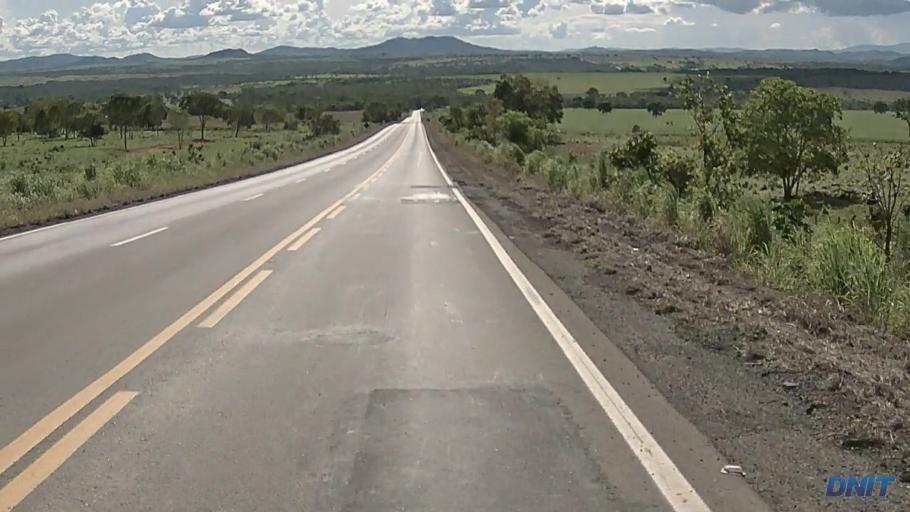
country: BR
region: Goias
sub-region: Padre Bernardo
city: Padre Bernardo
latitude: -15.2199
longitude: -48.5330
